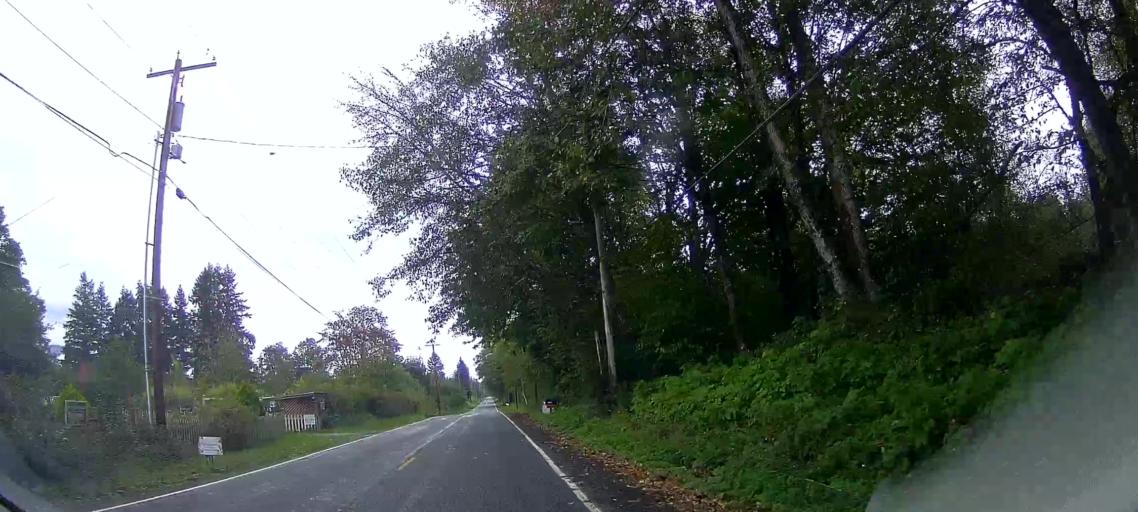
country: US
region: Washington
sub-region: Skagit County
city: Sedro-Woolley
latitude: 48.5274
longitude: -122.0486
